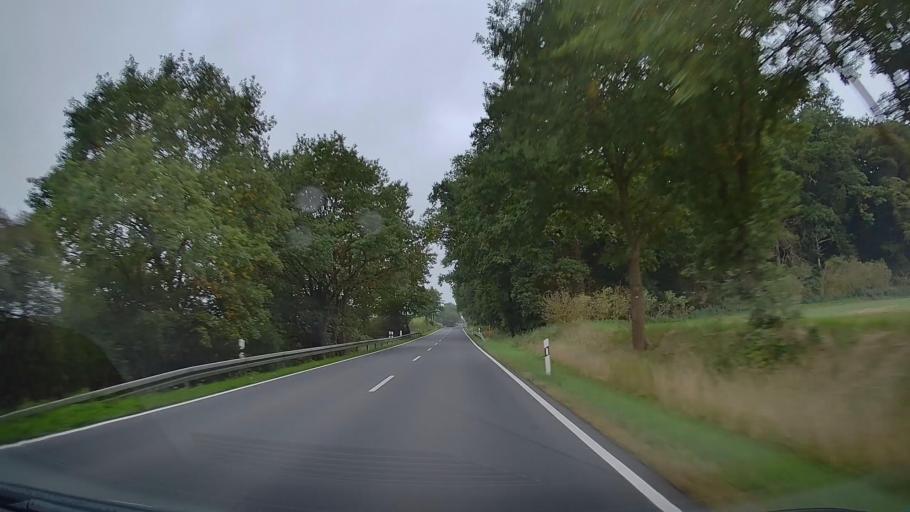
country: DE
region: Mecklenburg-Vorpommern
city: Tarnow
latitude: 53.7453
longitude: 12.0161
